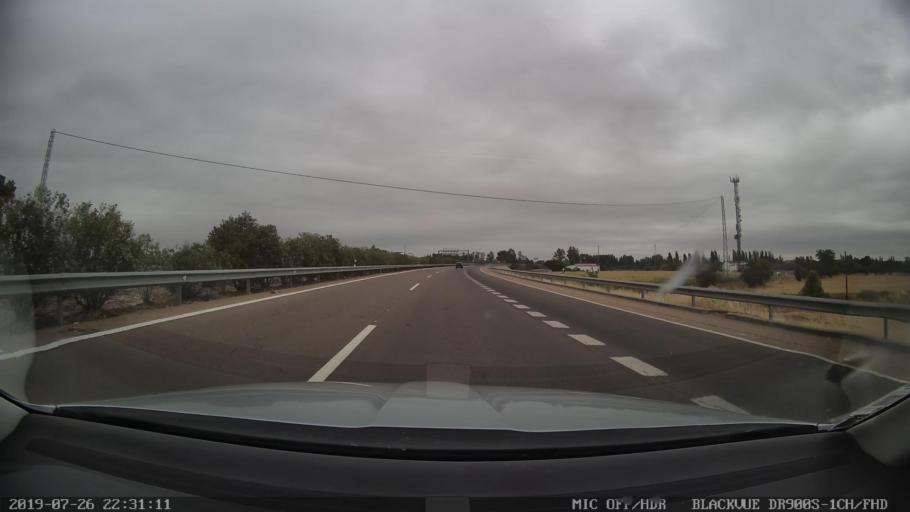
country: ES
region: Extremadura
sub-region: Provincia de Badajoz
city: Badajoz
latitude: 38.9206
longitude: -6.9620
